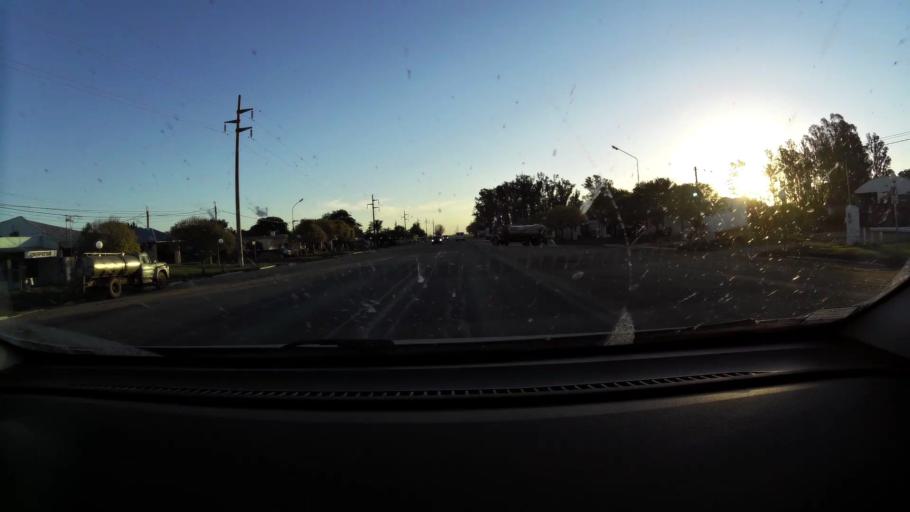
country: AR
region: Cordoba
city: La Playosa
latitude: -32.2017
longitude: -63.1608
